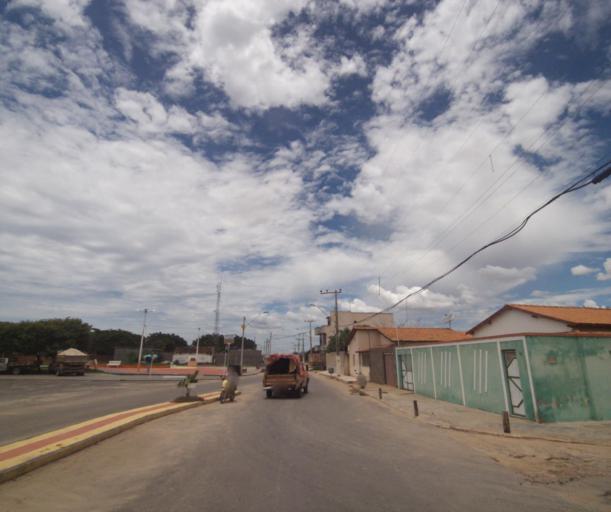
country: BR
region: Bahia
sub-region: Carinhanha
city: Carinhanha
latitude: -14.3343
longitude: -43.7716
